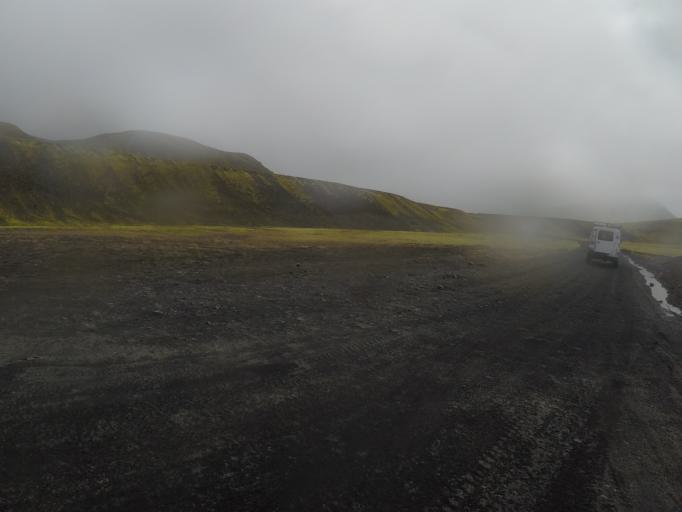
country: IS
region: South
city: Vestmannaeyjar
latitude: 63.9727
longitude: -18.7945
